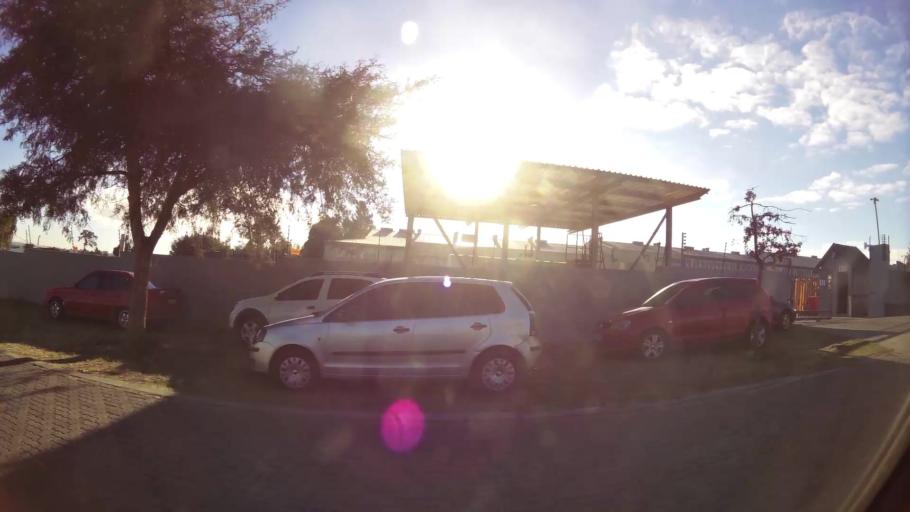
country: ZA
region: Gauteng
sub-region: City of Johannesburg Metropolitan Municipality
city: Midrand
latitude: -26.0390
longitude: 28.1461
